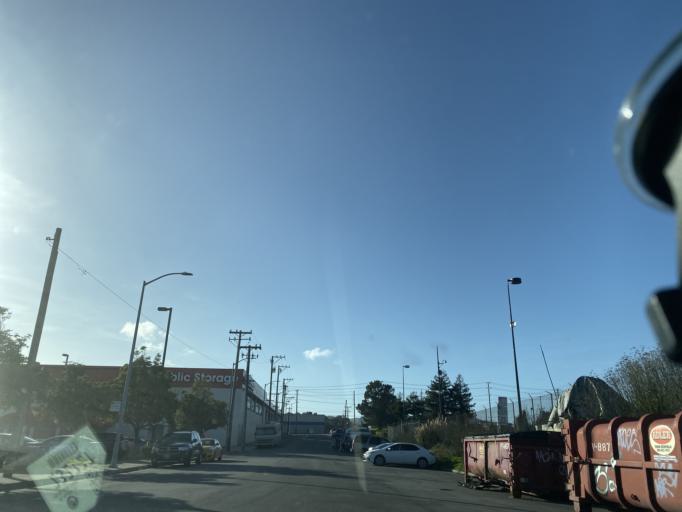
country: US
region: California
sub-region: San Francisco County
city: San Francisco
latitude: 37.7485
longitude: -122.3945
